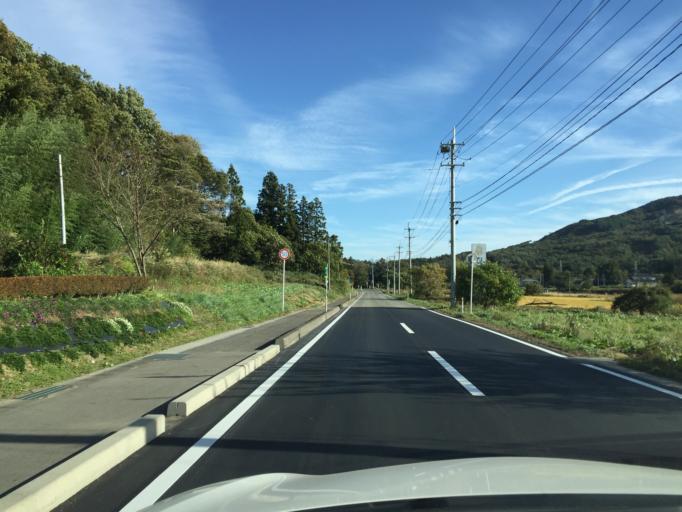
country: JP
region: Fukushima
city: Funehikimachi-funehiki
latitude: 37.3397
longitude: 140.5679
